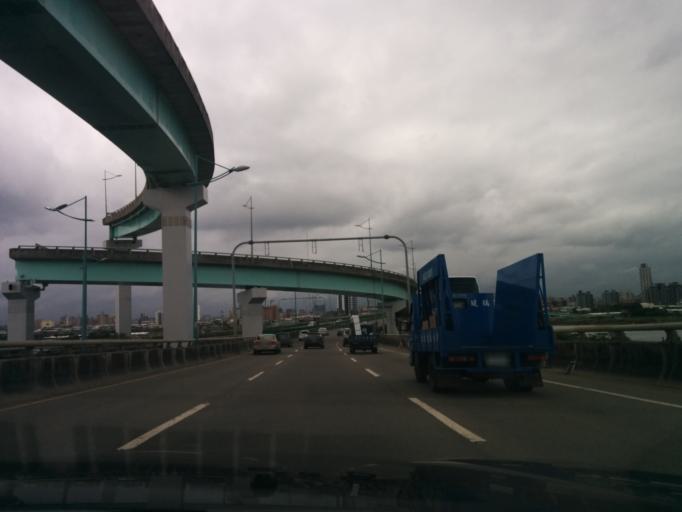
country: TW
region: Taipei
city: Taipei
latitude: 25.1028
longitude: 121.4989
